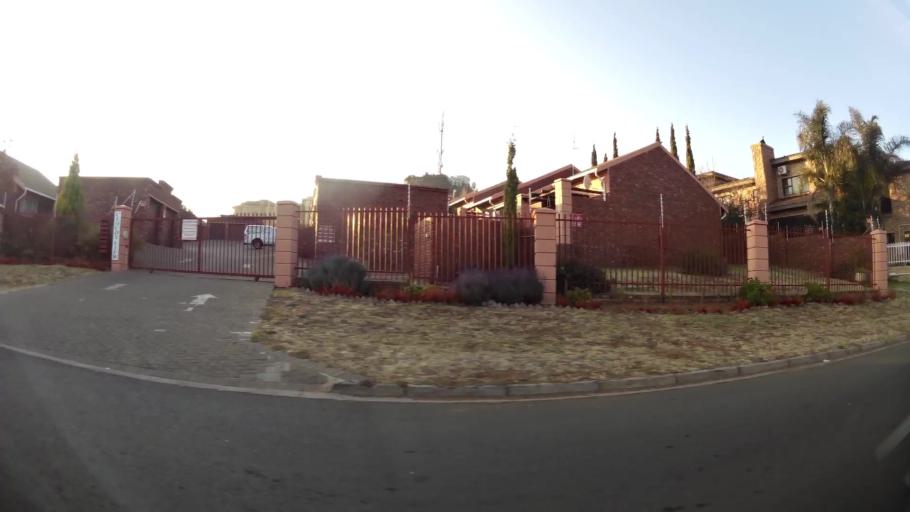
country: ZA
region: Orange Free State
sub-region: Mangaung Metropolitan Municipality
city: Bloemfontein
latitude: -29.0880
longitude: 26.1633
